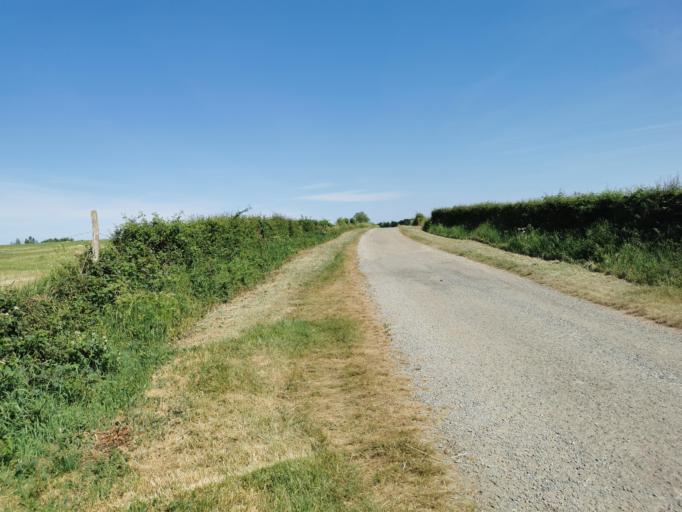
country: FR
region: Nord-Pas-de-Calais
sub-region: Departement du Nord
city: Marpent
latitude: 50.1820
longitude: 4.0861
